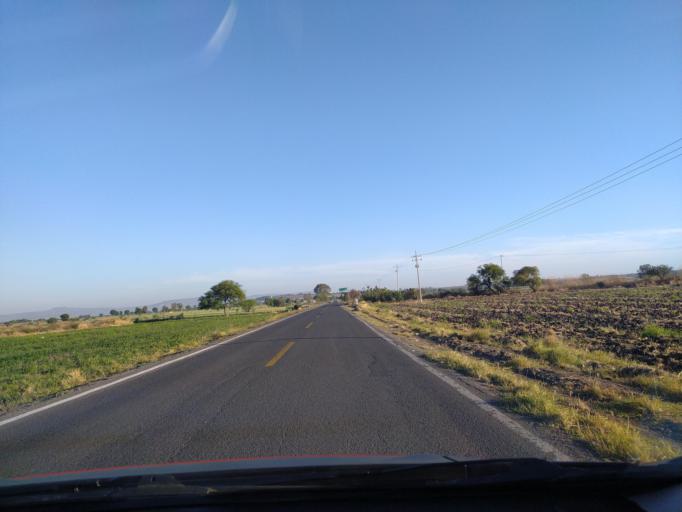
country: MX
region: Guanajuato
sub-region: San Francisco del Rincon
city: San Ignacio de Hidalgo
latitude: 20.8350
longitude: -101.8455
